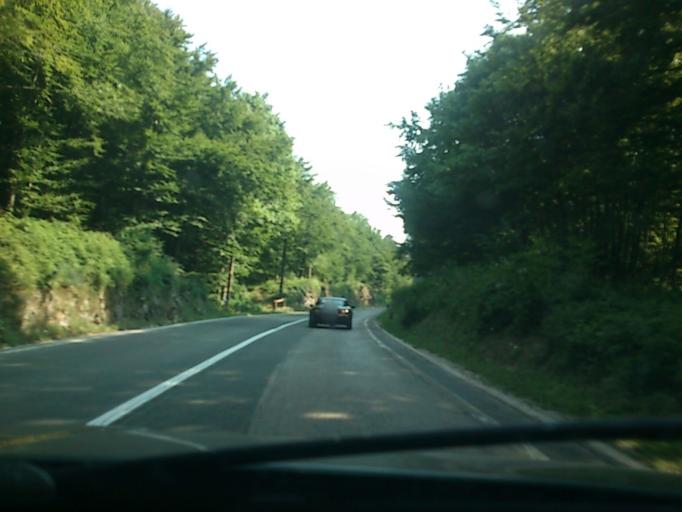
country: HR
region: Licko-Senjska
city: Jezerce
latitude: 44.8999
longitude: 15.6128
